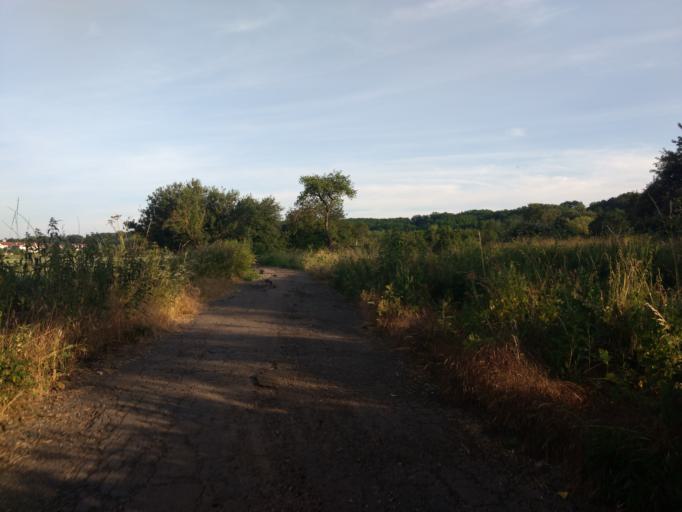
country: DE
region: Saarland
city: Wallerfangen
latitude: 49.3118
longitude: 6.7265
